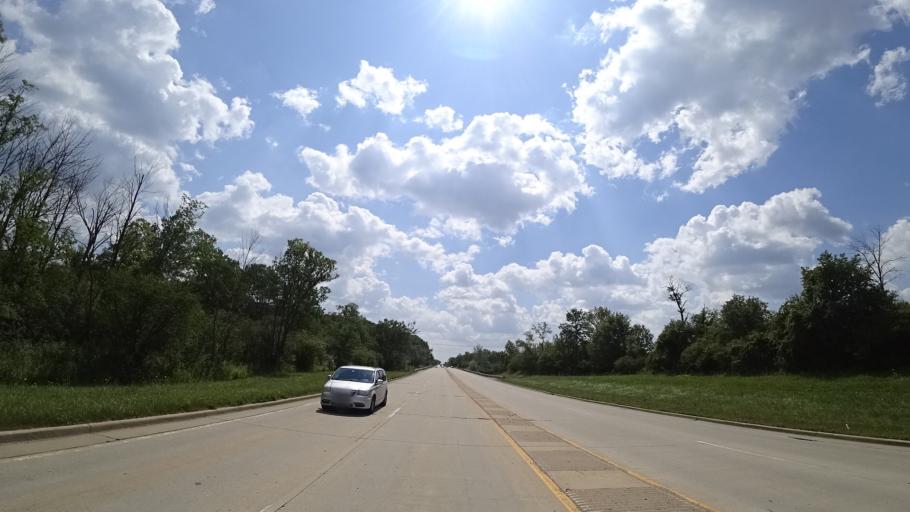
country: US
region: Illinois
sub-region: Cook County
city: Crestwood
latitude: 41.6446
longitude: -87.7768
